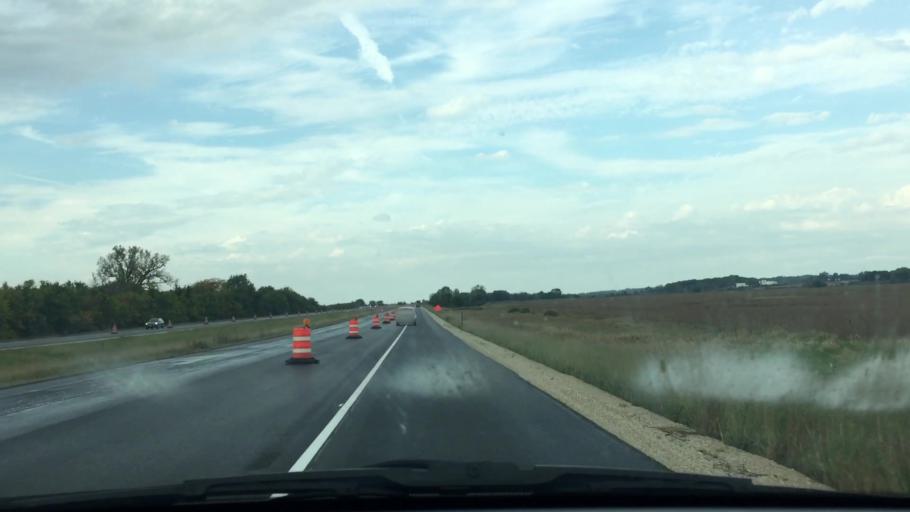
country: US
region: Illinois
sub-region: Whiteside County
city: Prophetstown
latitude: 41.7134
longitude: -90.0125
